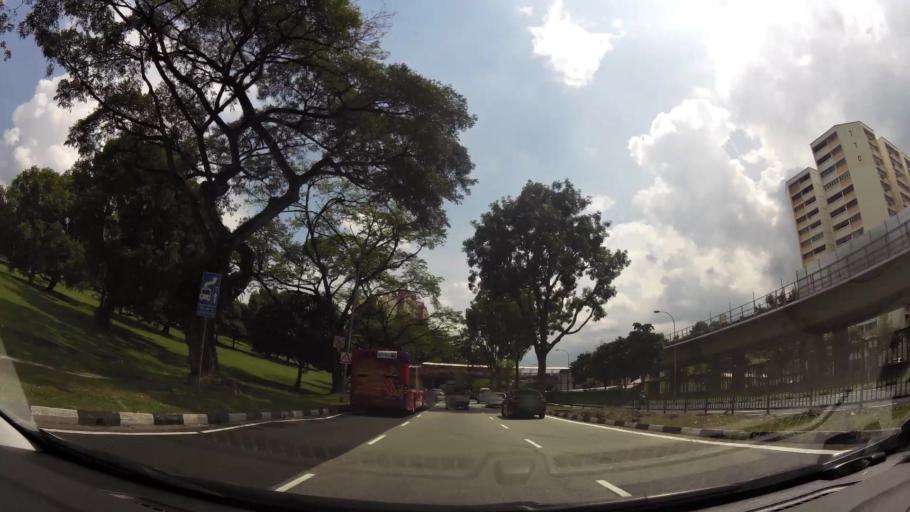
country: MY
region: Johor
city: Kampung Pasir Gudang Baru
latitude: 1.4380
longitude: 103.8333
